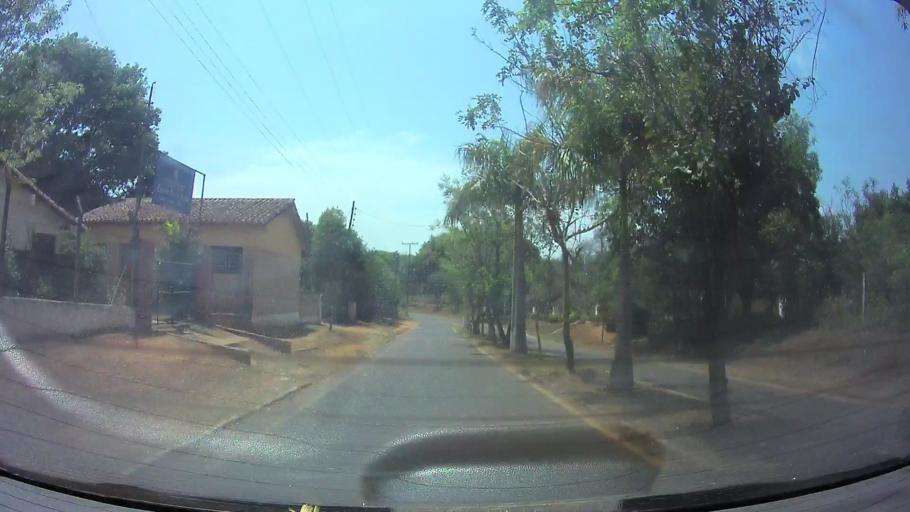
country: PY
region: Central
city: Ita
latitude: -25.4269
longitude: -57.3959
